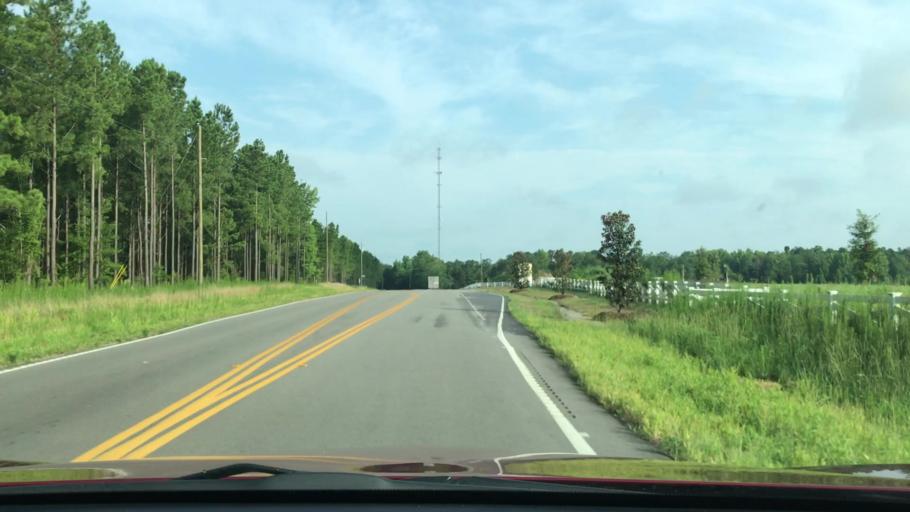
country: US
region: South Carolina
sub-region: Bamberg County
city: Denmark
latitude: 33.5367
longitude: -81.1337
